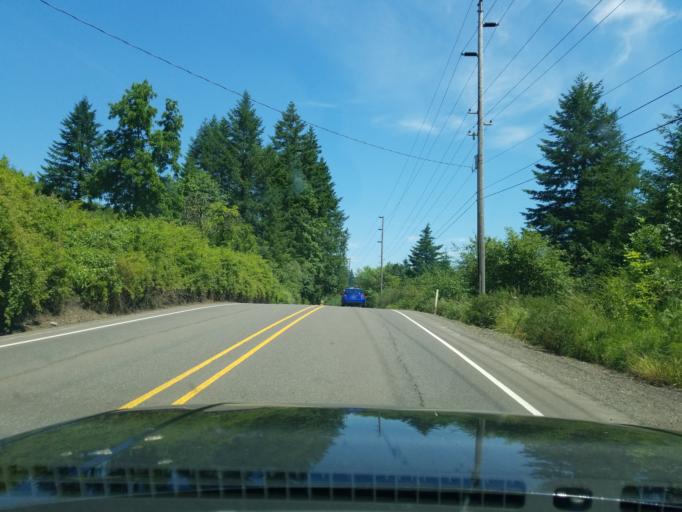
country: US
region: Oregon
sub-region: Yamhill County
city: Yamhill
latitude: 45.3873
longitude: -123.1384
